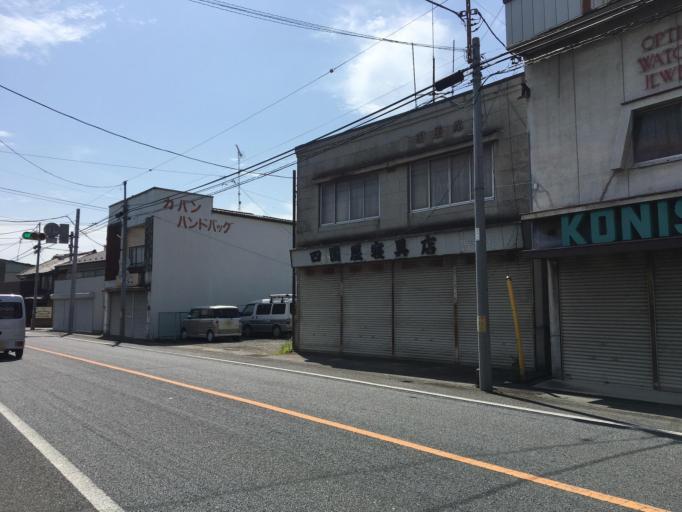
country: JP
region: Gunma
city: Sakai-nakajima
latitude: 36.2733
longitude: 139.2568
